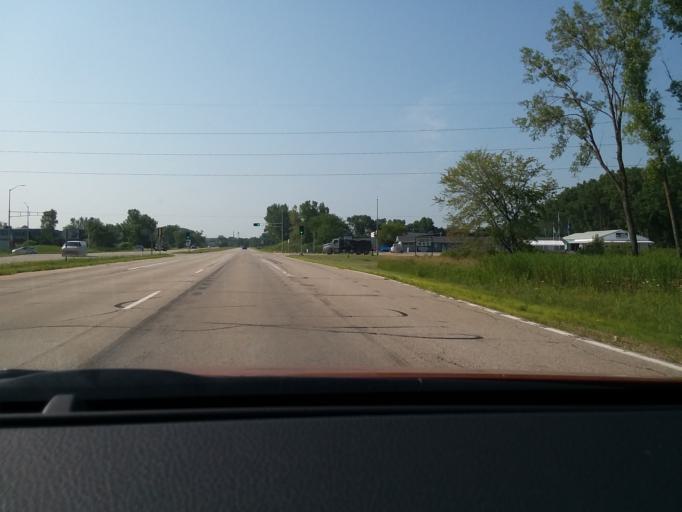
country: US
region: Wisconsin
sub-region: Dane County
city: Maple Bluff
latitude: 43.1602
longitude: -89.4058
